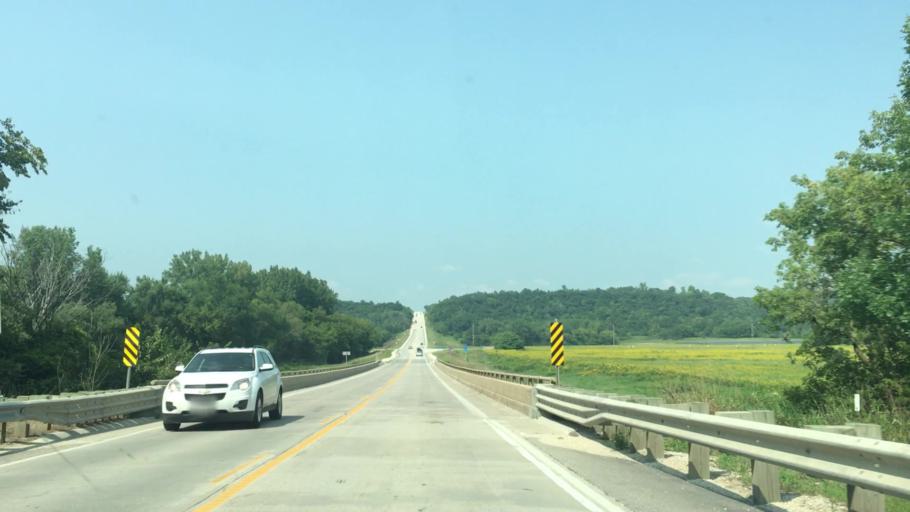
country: US
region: Iowa
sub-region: Winneshiek County
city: Decorah
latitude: 43.3152
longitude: -91.8144
